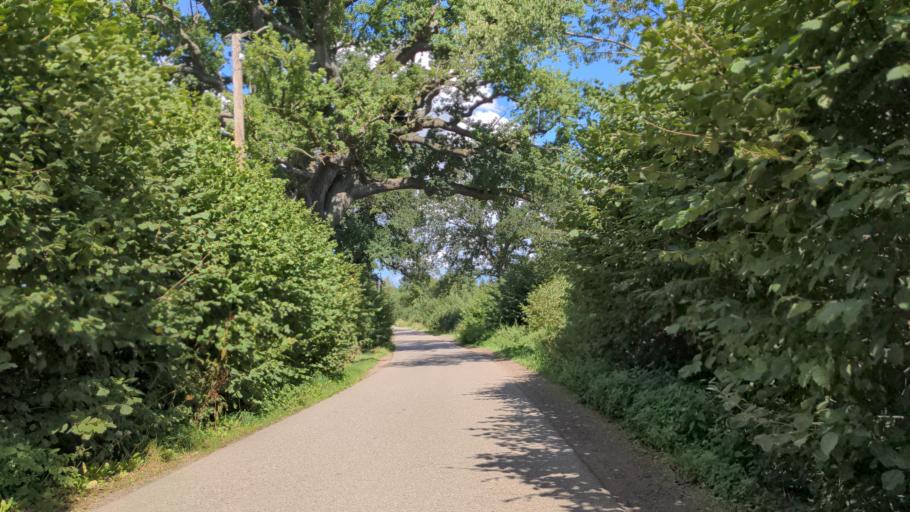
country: DE
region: Schleswig-Holstein
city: Beschendorf
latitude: 54.1872
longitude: 10.8244
